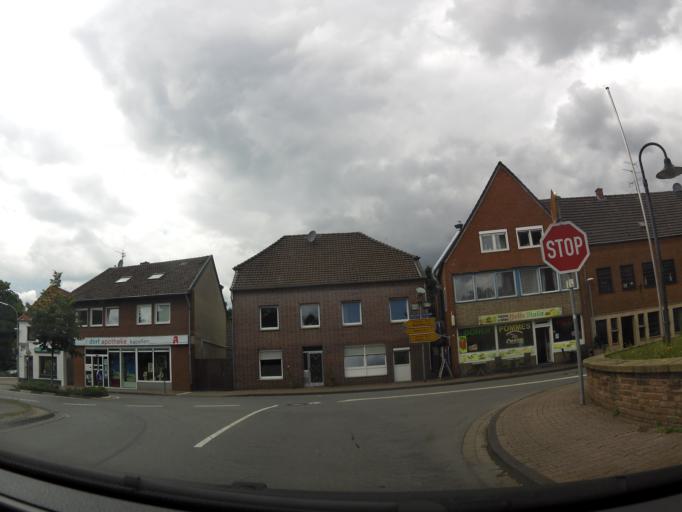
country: DE
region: North Rhine-Westphalia
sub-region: Regierungsbezirk Dusseldorf
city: Sonsbeck
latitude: 51.5710
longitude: 6.3631
